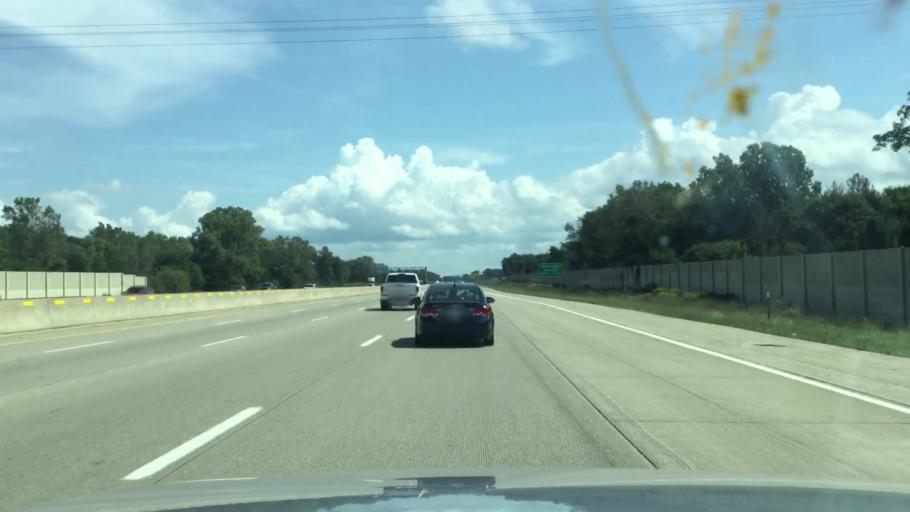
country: US
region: Michigan
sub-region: Kalamazoo County
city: Portage
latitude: 42.2378
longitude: -85.6295
